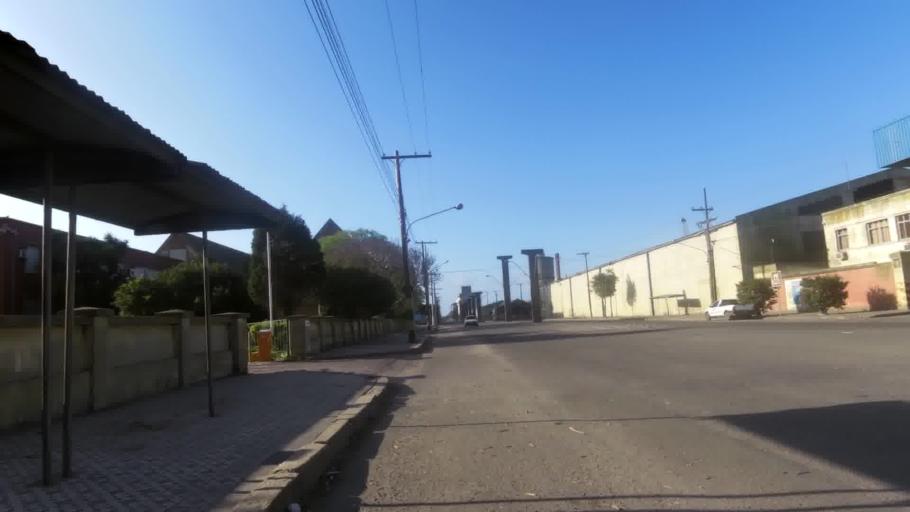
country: BR
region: Rio Grande do Sul
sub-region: Rio Grande
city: Rio Grande
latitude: -32.0426
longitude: -52.0767
